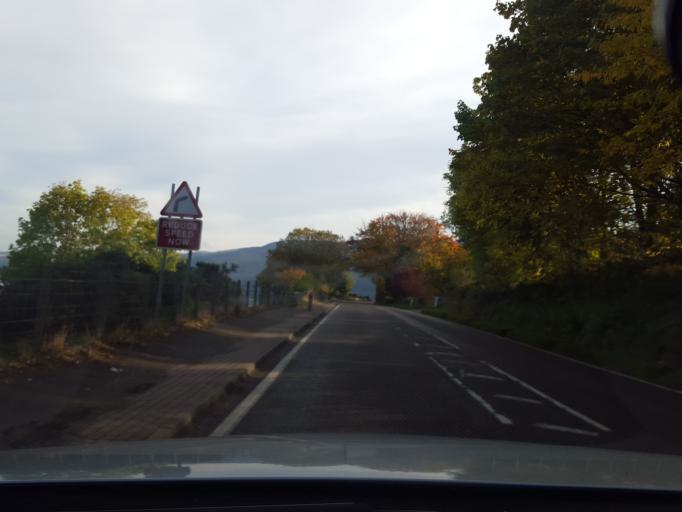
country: GB
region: Scotland
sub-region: Highland
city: Beauly
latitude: 57.3272
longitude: -4.4495
